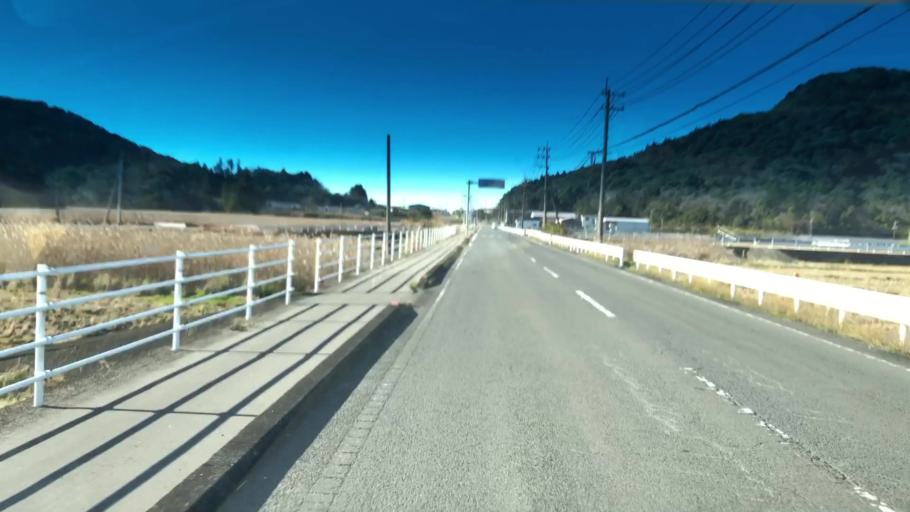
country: JP
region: Kagoshima
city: Satsumasendai
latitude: 31.8174
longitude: 130.2695
